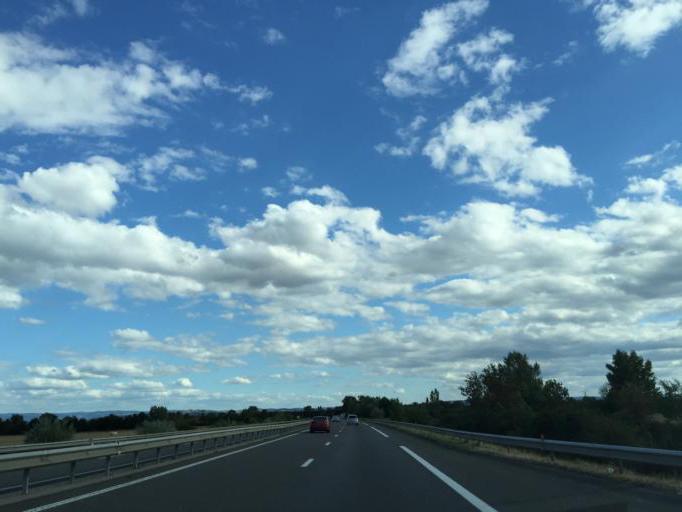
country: FR
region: Rhone-Alpes
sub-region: Departement de la Loire
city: Cuzieu
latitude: 45.5857
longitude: 4.2123
